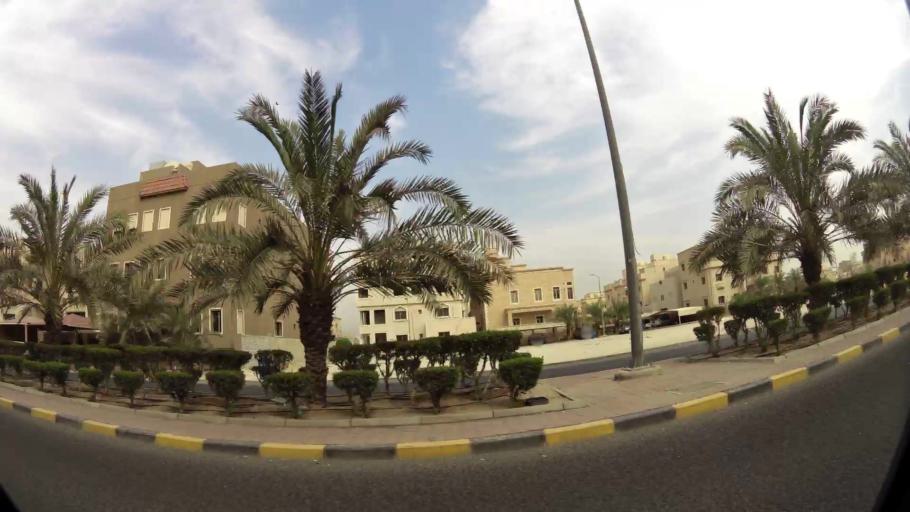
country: KW
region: Mubarak al Kabir
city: Sabah as Salim
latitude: 29.2712
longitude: 48.0263
